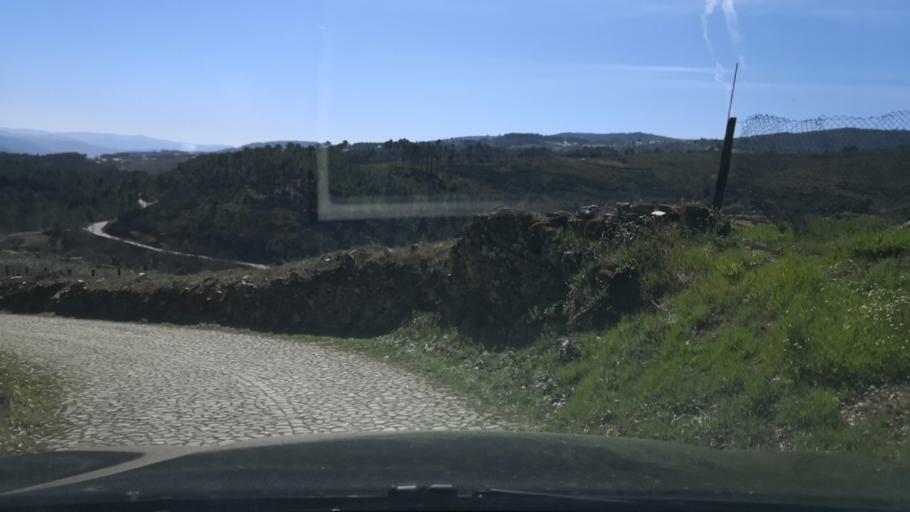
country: PT
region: Vila Real
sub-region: Sabrosa
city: Sabrosa
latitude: 41.3348
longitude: -7.5860
